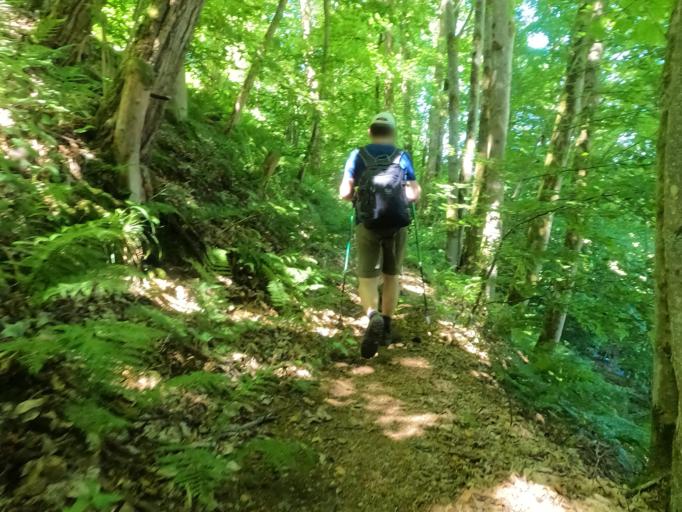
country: DE
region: Rheinland-Pfalz
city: Alpenrod
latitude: 50.6602
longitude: 7.8783
